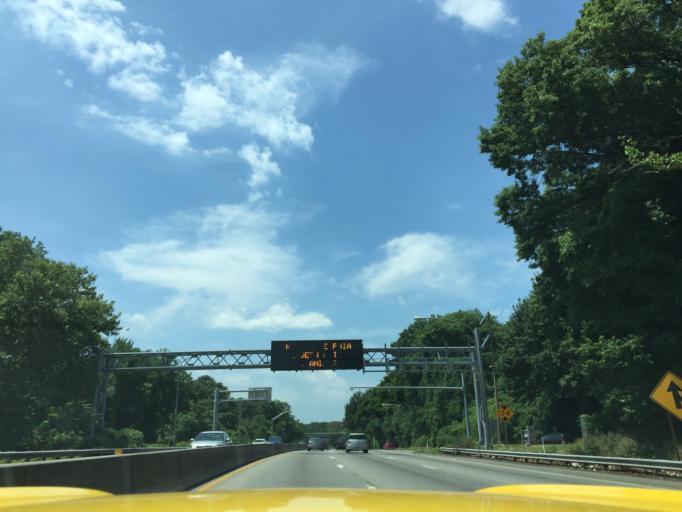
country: US
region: Pennsylvania
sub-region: Philadelphia County
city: Philadelphia
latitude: 40.0187
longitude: -75.1665
